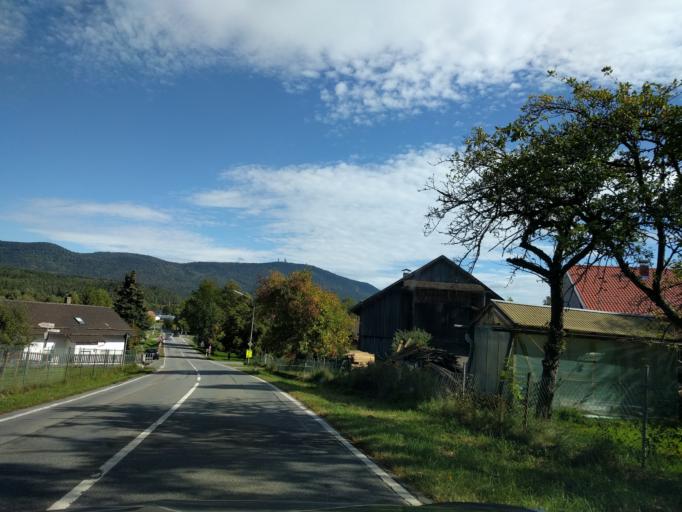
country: DE
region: Bavaria
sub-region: Upper Palatinate
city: Grafenwiesen
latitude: 49.2005
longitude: 12.8764
